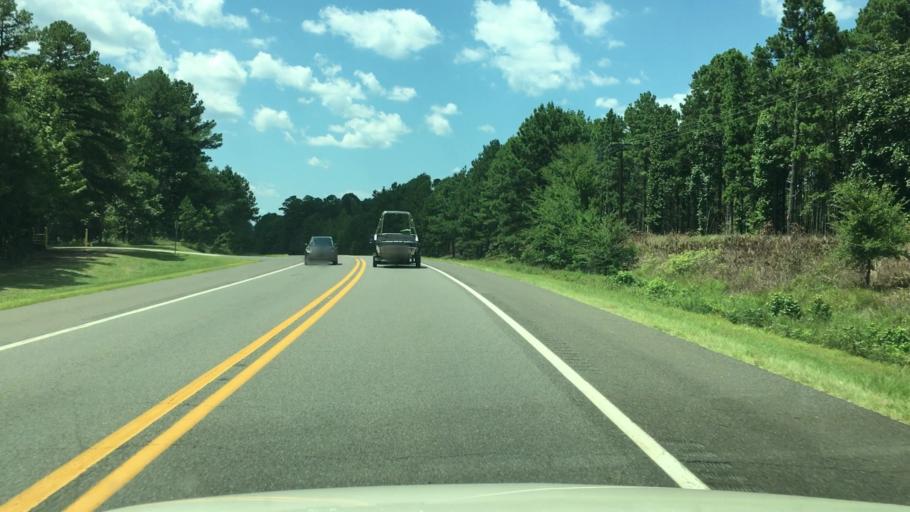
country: US
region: Arkansas
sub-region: Clark County
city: Arkadelphia
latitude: 34.2288
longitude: -93.0914
